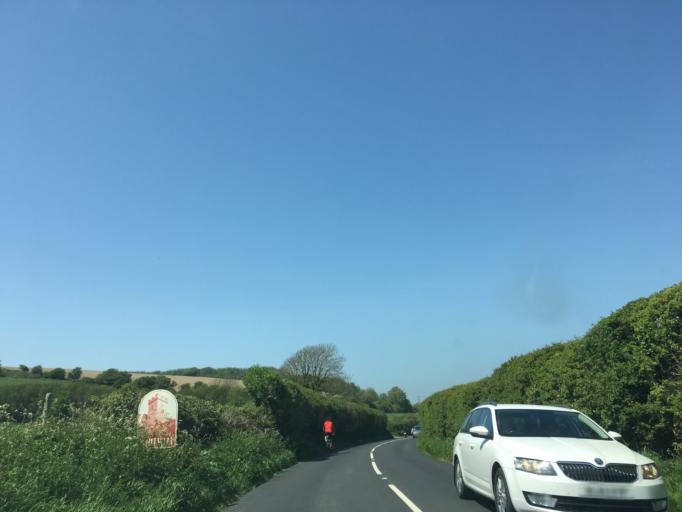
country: GB
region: England
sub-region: Isle of Wight
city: Niton
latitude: 50.5921
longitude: -1.2599
